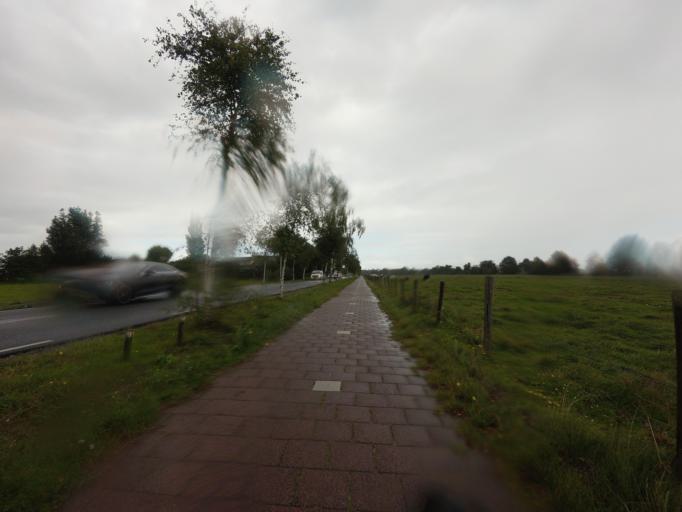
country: NL
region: North Holland
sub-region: Gemeente Wijdemeren
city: Nieuw-Loosdrecht
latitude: 52.1635
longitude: 5.1683
